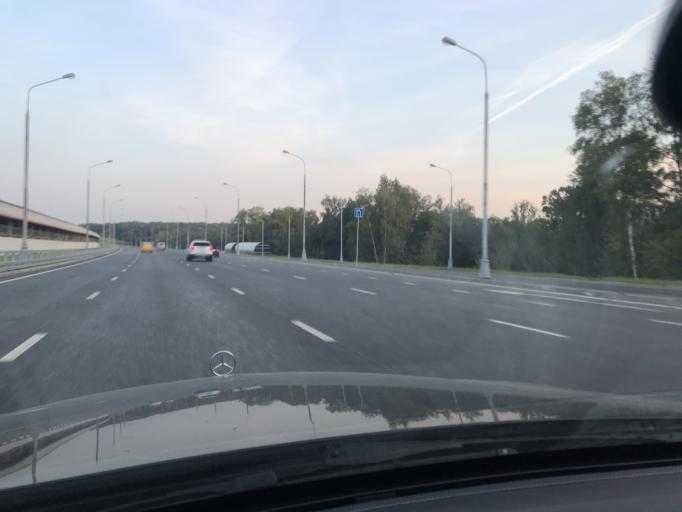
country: RU
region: Moskovskaya
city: Mosrentgen
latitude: 55.5921
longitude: 37.4211
